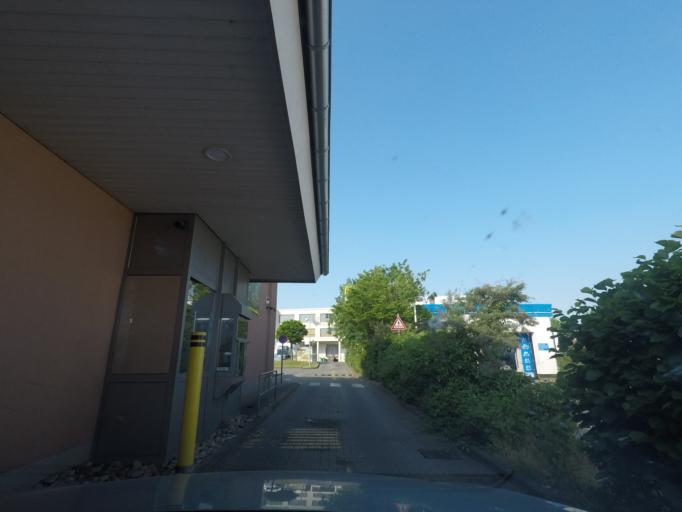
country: DE
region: Brandenburg
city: Schulzendorf
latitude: 52.3666
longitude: 13.5629
